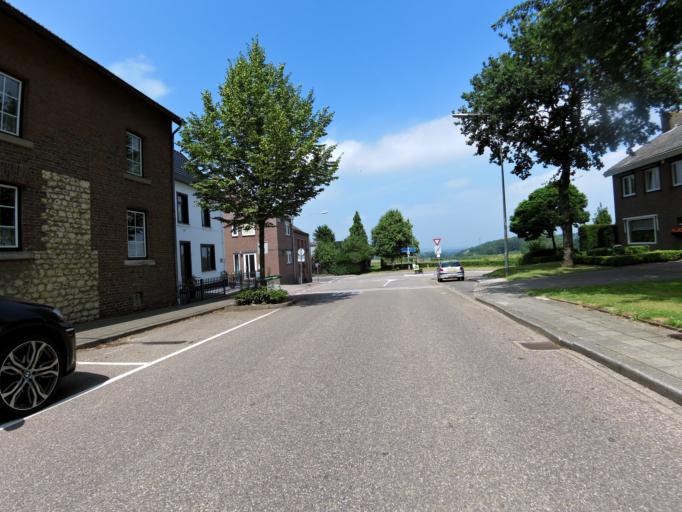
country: NL
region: Limburg
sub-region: Gemeente Simpelveld
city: Simpelveld
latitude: 50.8456
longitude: 5.9689
